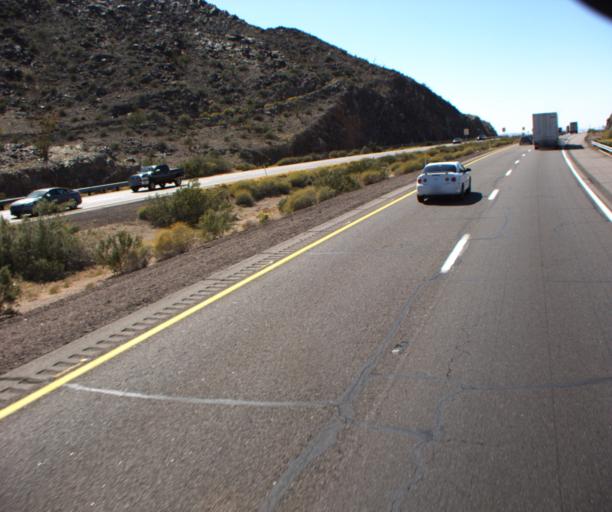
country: US
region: Arizona
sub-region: Yuma County
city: Wellton
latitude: 32.7260
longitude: -113.7451
